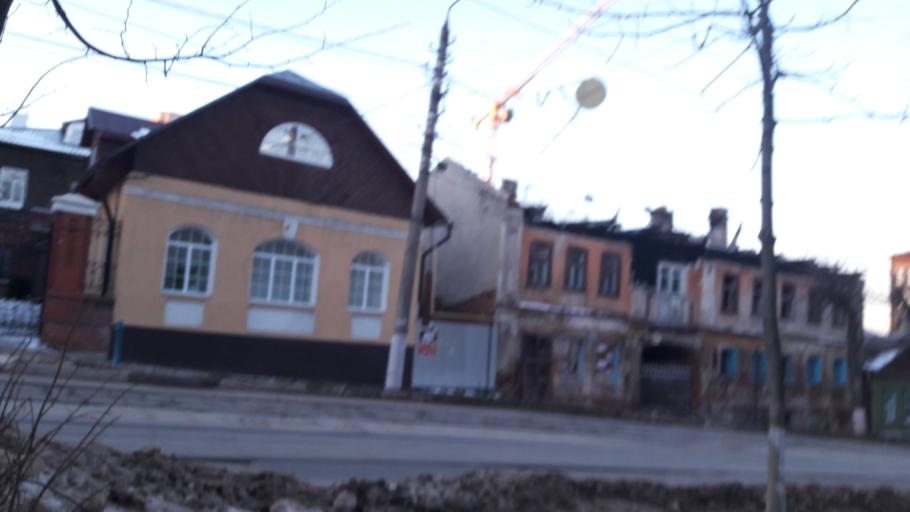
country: RU
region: Tula
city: Tula
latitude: 54.1871
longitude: 37.6072
